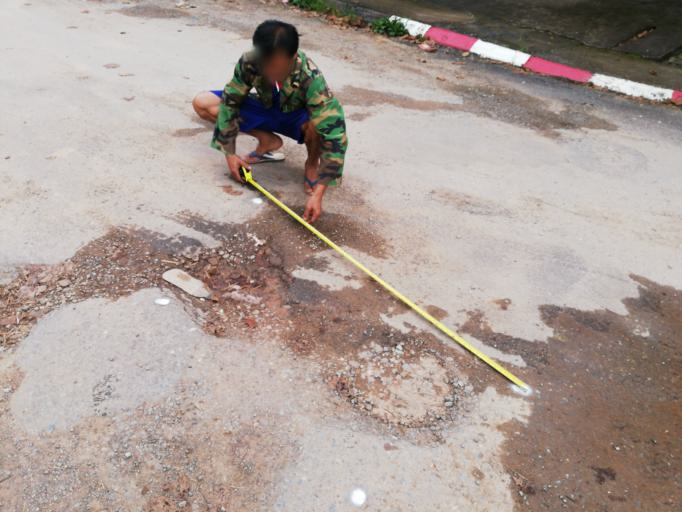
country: LA
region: Loungnamtha
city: Louang Namtha
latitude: 21.0045
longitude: 101.4074
